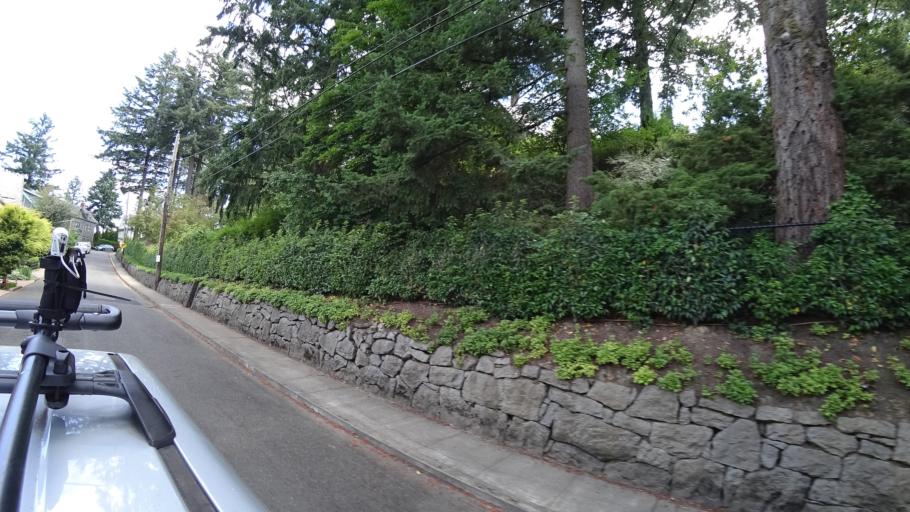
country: US
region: Oregon
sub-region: Multnomah County
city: Portland
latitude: 45.5087
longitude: -122.7053
